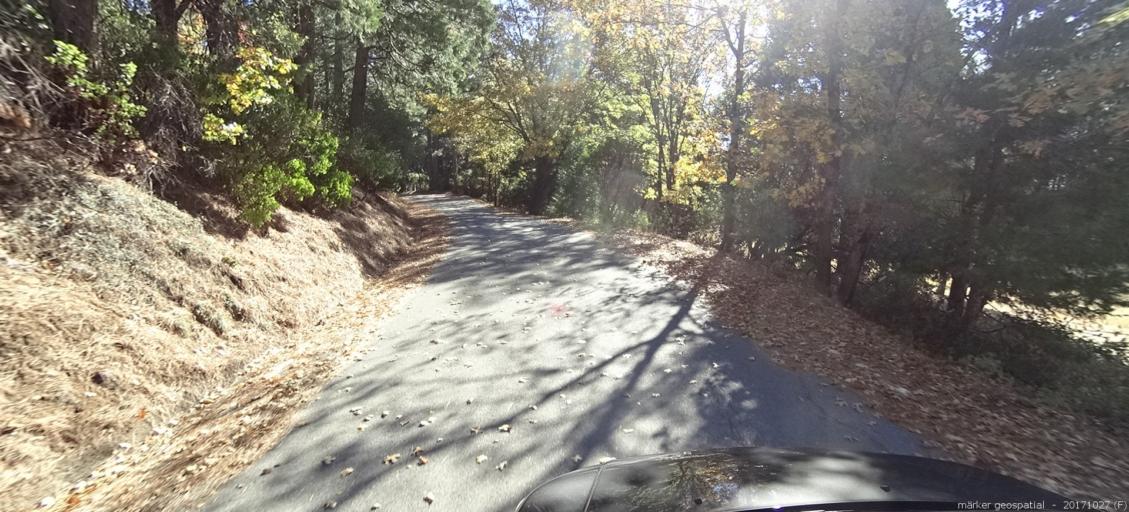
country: US
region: California
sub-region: Shasta County
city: Burney
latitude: 40.8049
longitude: -121.8994
